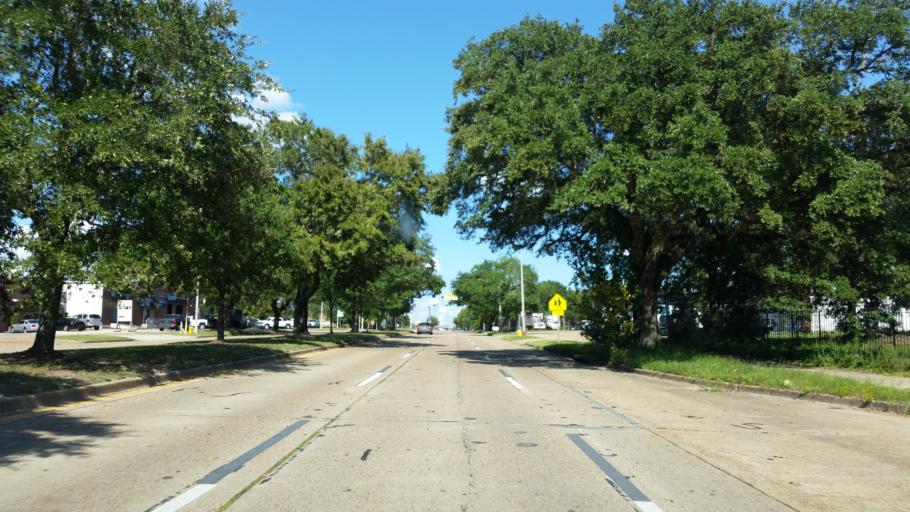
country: US
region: Alabama
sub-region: Mobile County
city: Mobile
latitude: 30.6970
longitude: -88.0535
